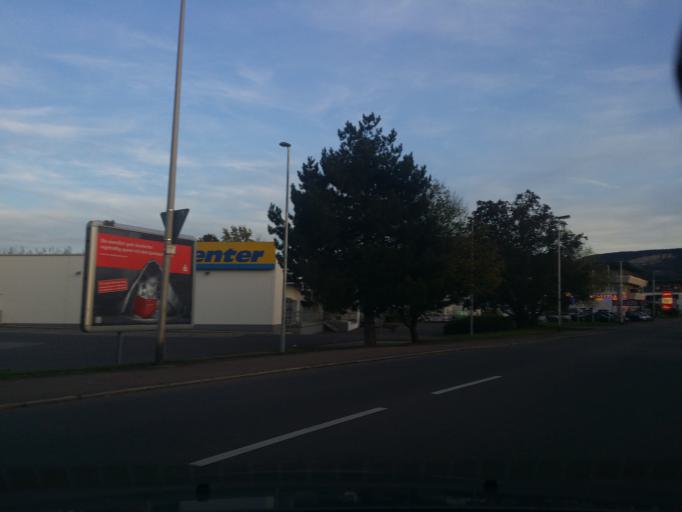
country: DE
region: Baden-Wuerttemberg
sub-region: Tuebingen Region
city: Ofterdingen
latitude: 48.4071
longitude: 9.0381
